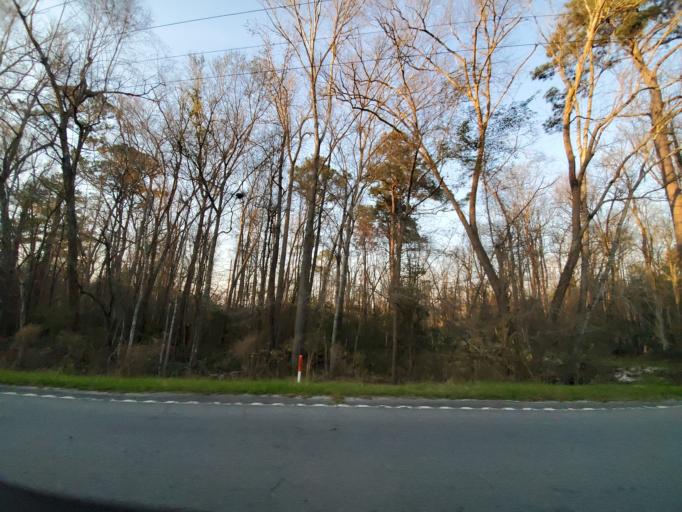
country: US
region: South Carolina
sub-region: Dorchester County
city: Saint George
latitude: 33.0469
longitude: -80.5406
